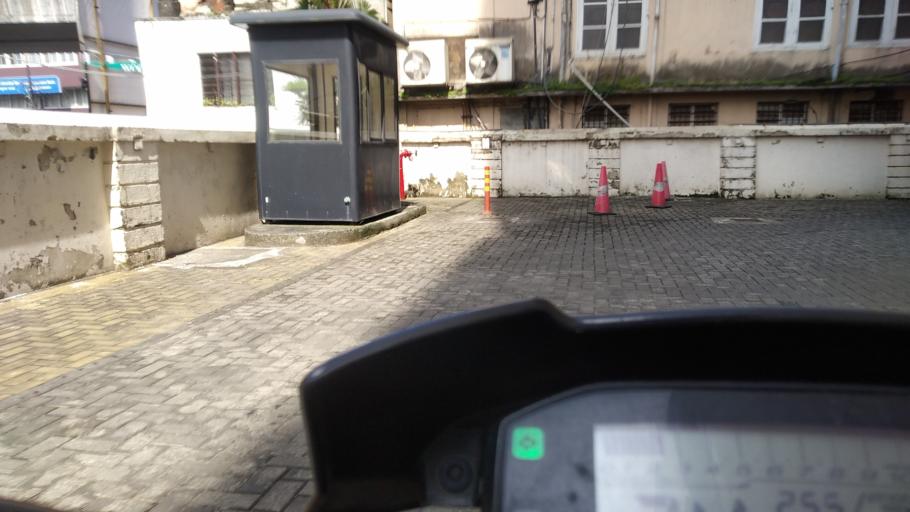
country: IN
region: Kerala
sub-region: Ernakulam
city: Cochin
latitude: 9.9781
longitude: 76.2833
